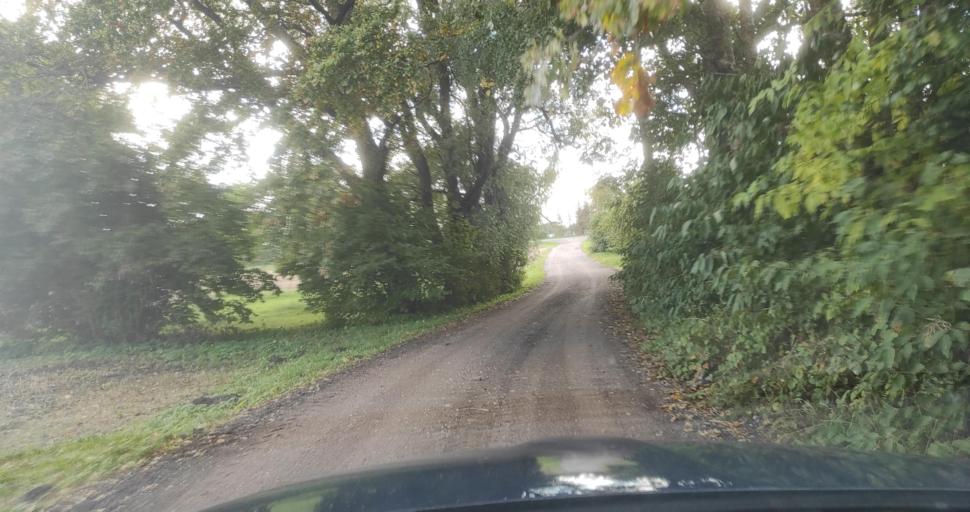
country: LV
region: Ventspils Rajons
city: Piltene
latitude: 57.2641
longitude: 21.6034
